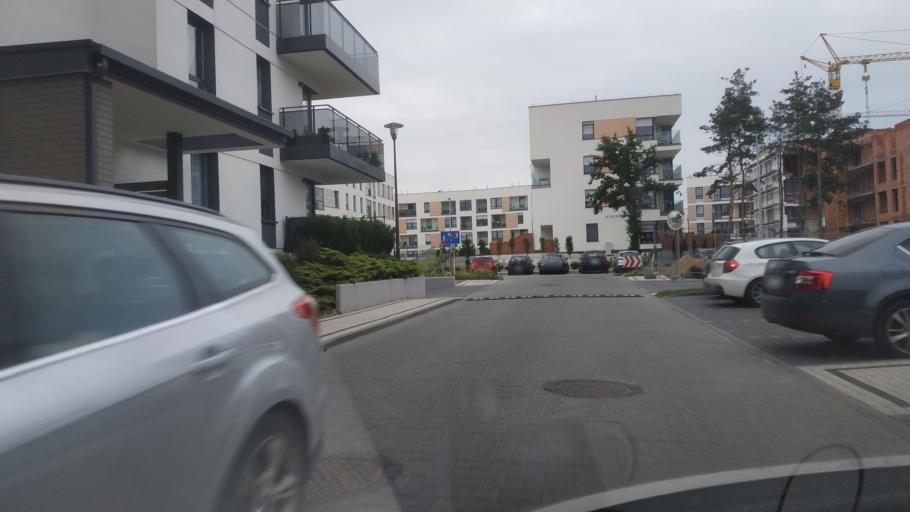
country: PL
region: Kujawsko-Pomorskie
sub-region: Torun
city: Torun
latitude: 53.0460
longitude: 18.6048
